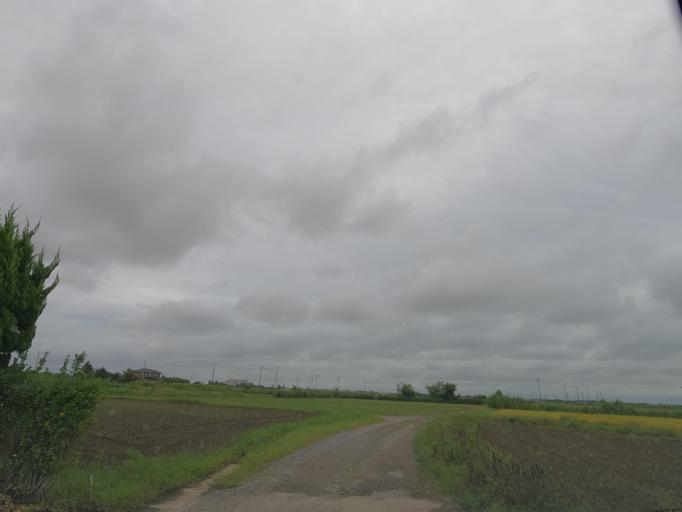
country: JP
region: Ibaraki
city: Toride
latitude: 35.9311
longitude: 140.0612
